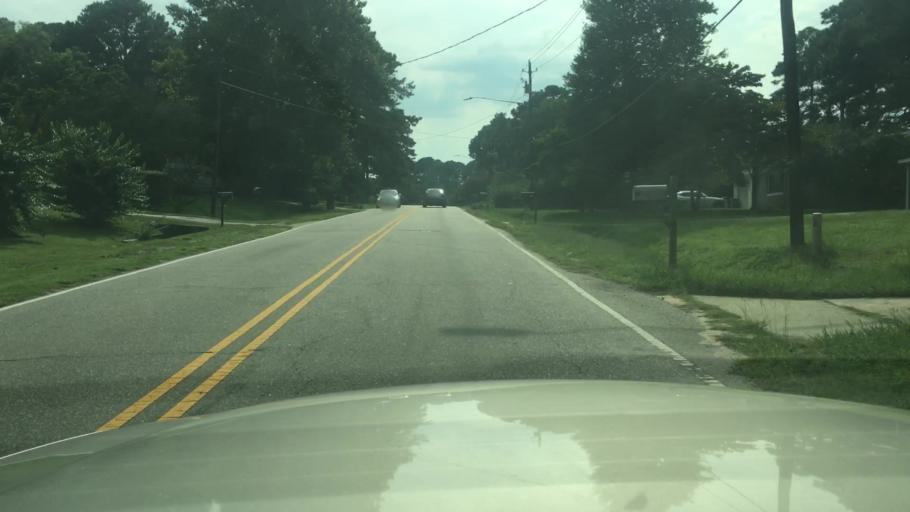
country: US
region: North Carolina
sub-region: Cumberland County
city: Fort Bragg
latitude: 35.1028
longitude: -79.0029
